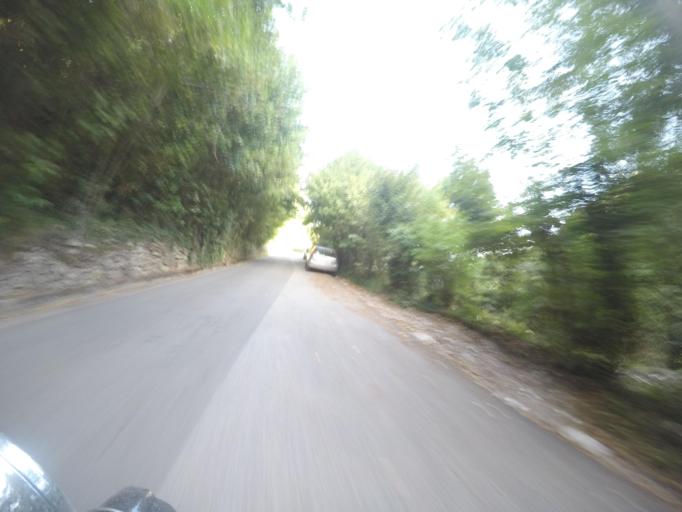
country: IT
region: Tuscany
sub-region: Provincia di Massa-Carrara
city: Carrara
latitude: 44.0834
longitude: 10.0908
